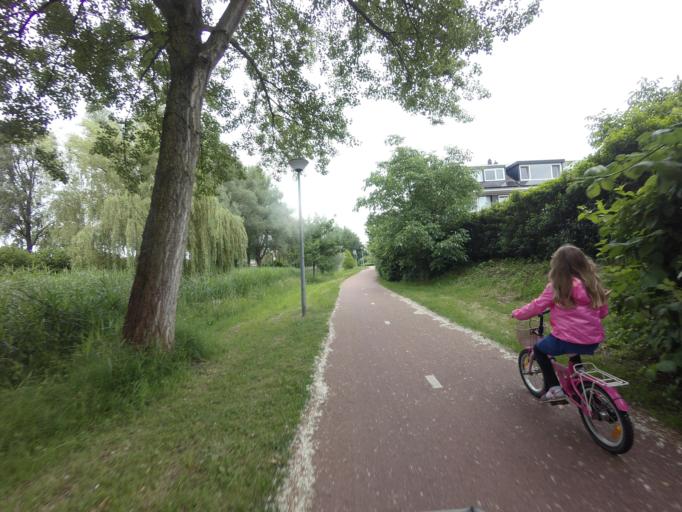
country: NL
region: North Holland
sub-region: Gemeente Huizen
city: Huizen
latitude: 52.2967
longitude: 5.2757
